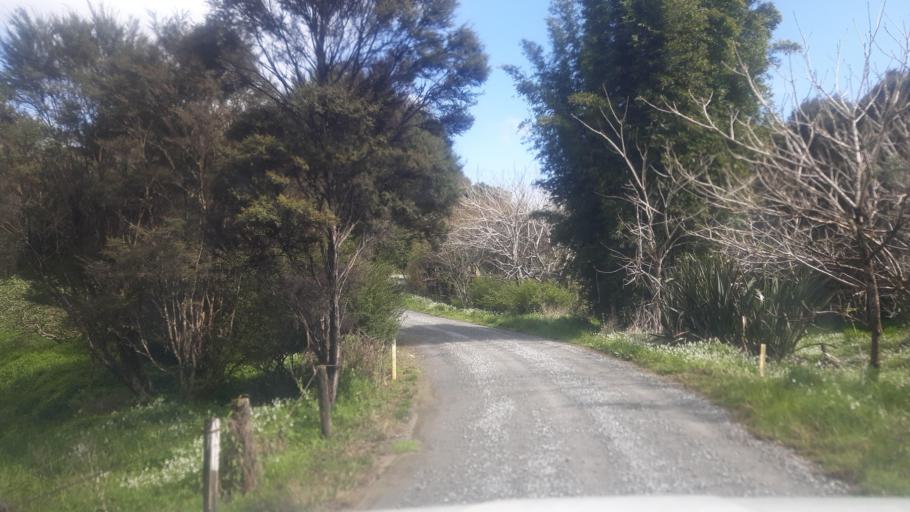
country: NZ
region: Northland
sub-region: Far North District
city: Taipa
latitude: -35.1159
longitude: 173.4322
